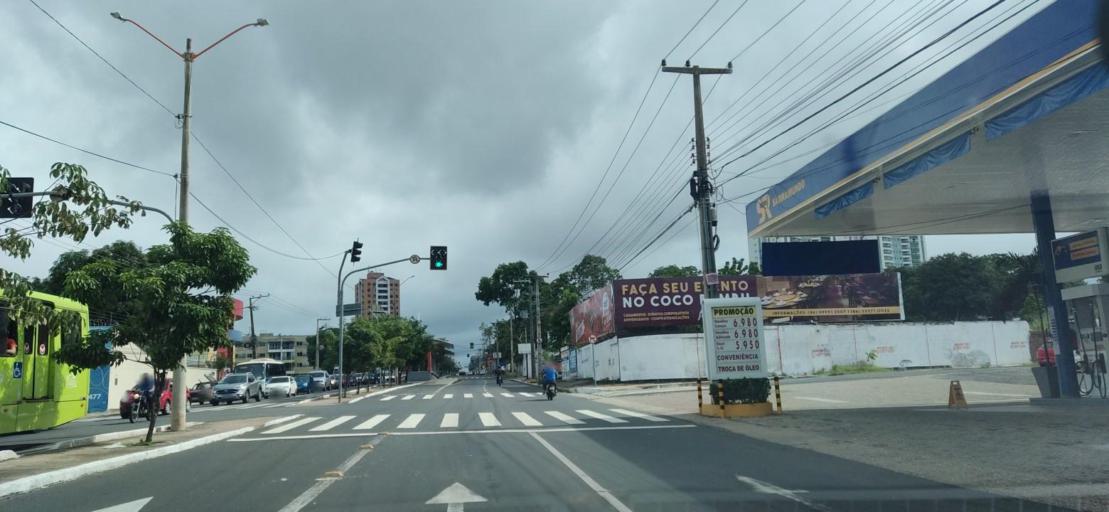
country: BR
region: Piaui
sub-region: Teresina
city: Teresina
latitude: -5.0695
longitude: -42.7714
